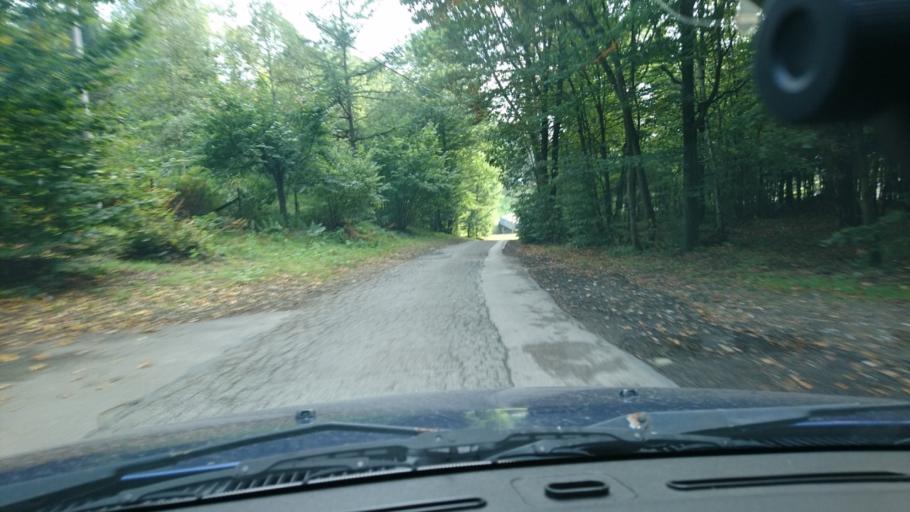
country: PL
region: Silesian Voivodeship
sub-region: Powiat bielski
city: Wilkowice
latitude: 49.7613
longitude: 19.1151
